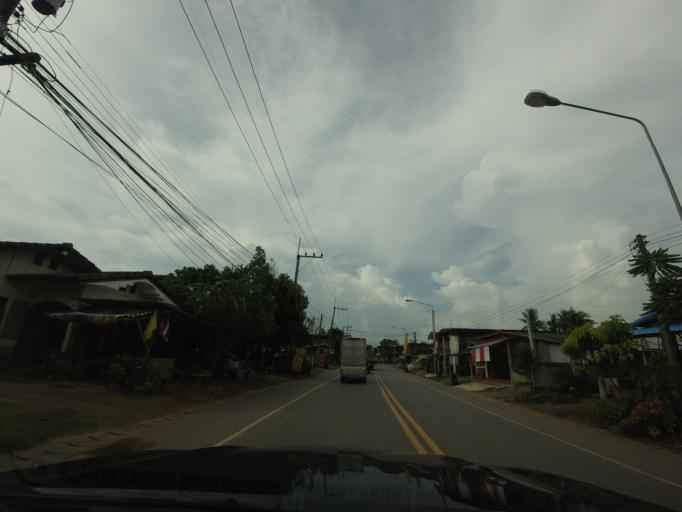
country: TH
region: Changwat Nong Bua Lamphu
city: Suwannakhuha
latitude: 17.4679
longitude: 102.3473
